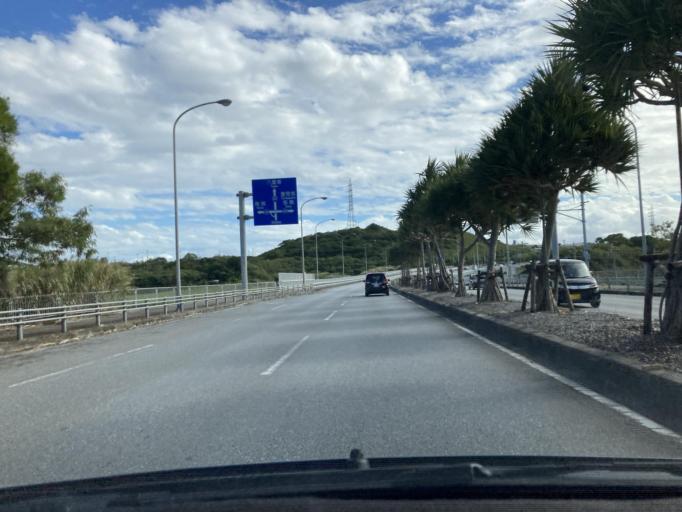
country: JP
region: Okinawa
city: Tomigusuku
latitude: 26.1786
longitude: 127.7264
